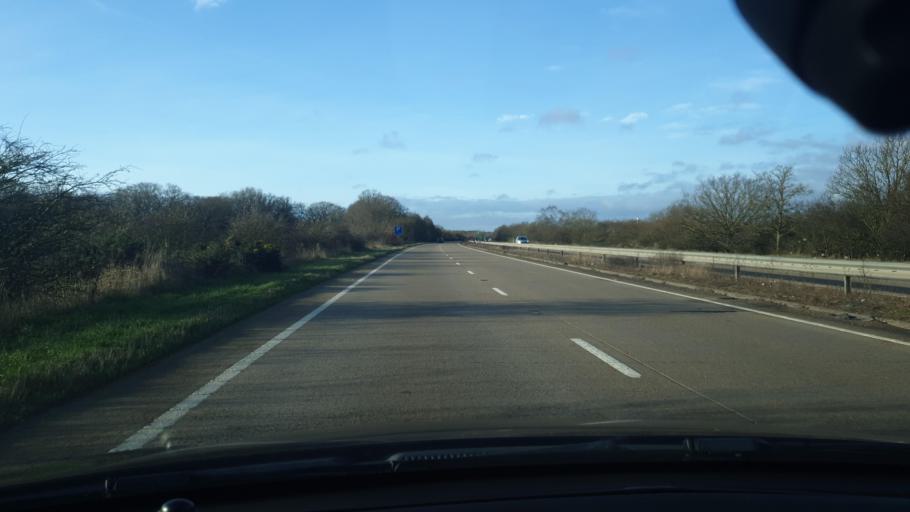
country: GB
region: England
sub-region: Essex
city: Alresford
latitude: 51.8995
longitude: 0.9856
